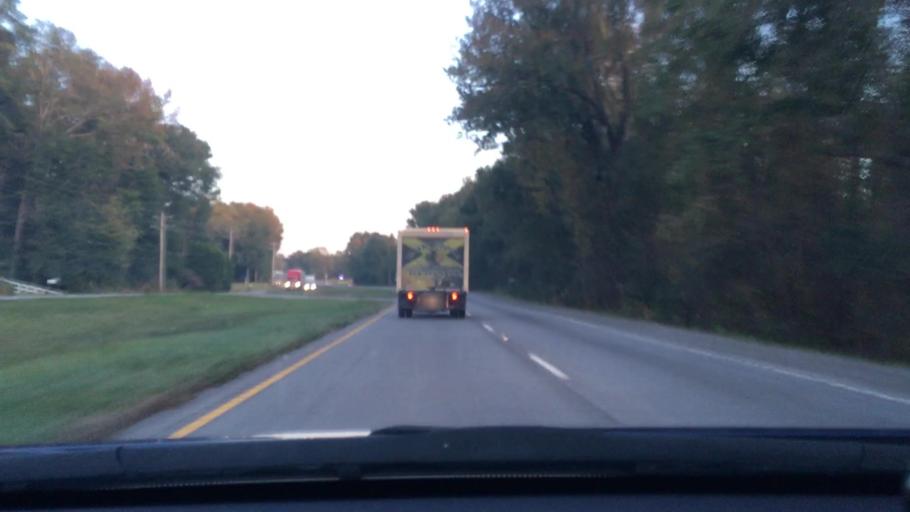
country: US
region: South Carolina
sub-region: Richland County
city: Gadsden
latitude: 33.9446
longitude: -80.7522
